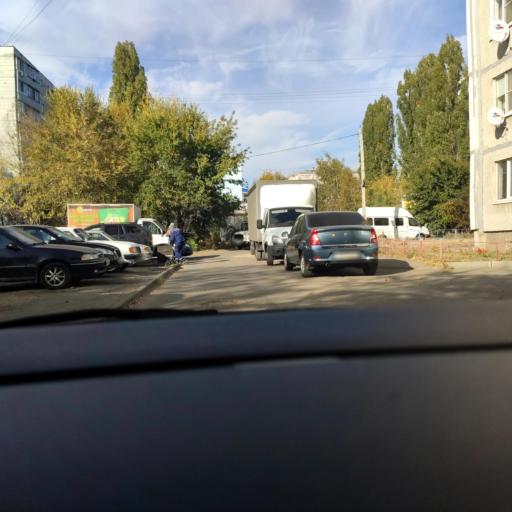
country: RU
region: Voronezj
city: Podgornoye
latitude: 51.7109
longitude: 39.1676
